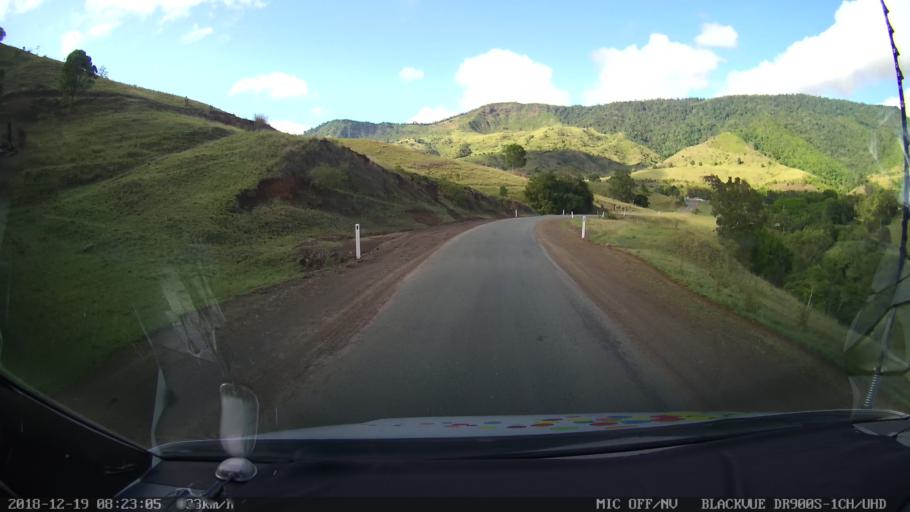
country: AU
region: New South Wales
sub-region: Kyogle
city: Kyogle
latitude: -28.3056
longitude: 152.9113
